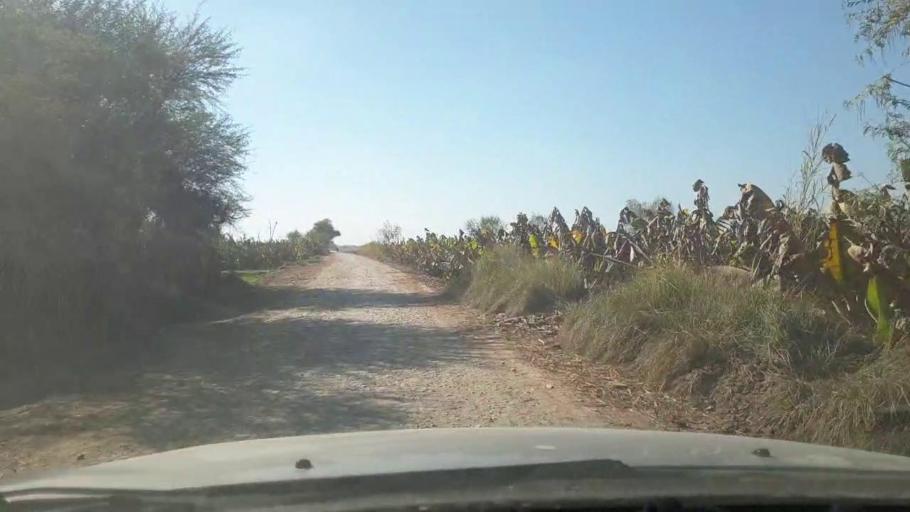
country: PK
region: Sindh
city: Ghotki
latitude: 27.9846
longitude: 69.2206
